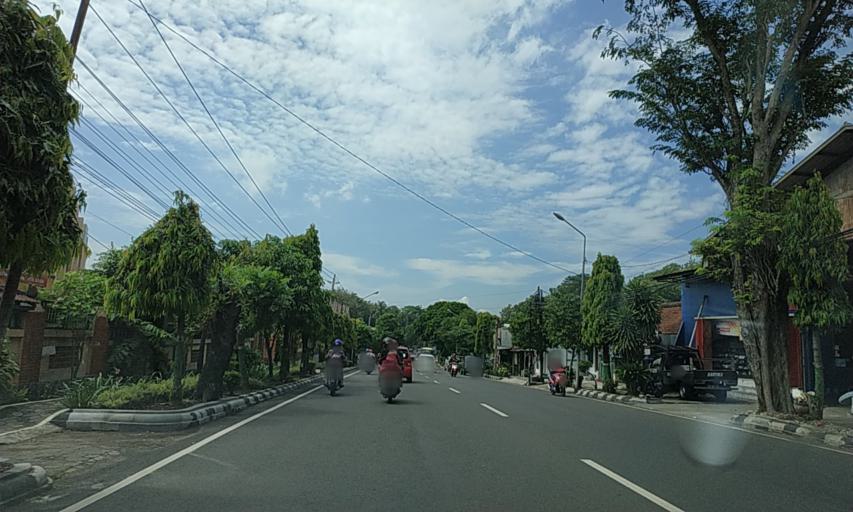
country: ID
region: Central Java
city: Selogiri
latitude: -7.8050
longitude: 110.9202
